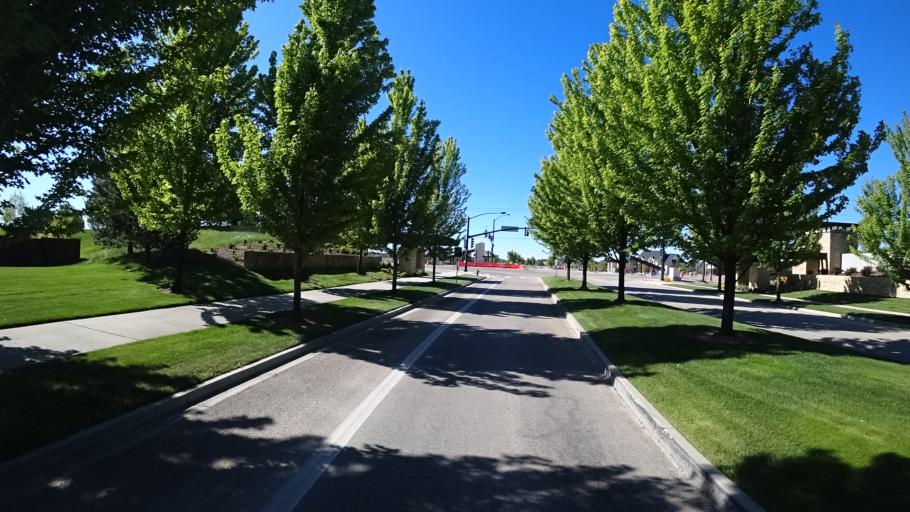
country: US
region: Idaho
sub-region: Ada County
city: Star
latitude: 43.6634
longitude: -116.4436
